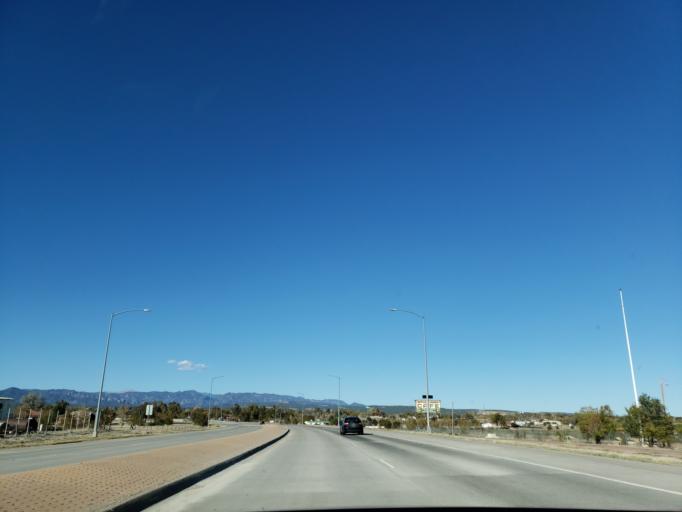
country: US
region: Colorado
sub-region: Fremont County
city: Penrose
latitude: 38.4291
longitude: -105.0246
